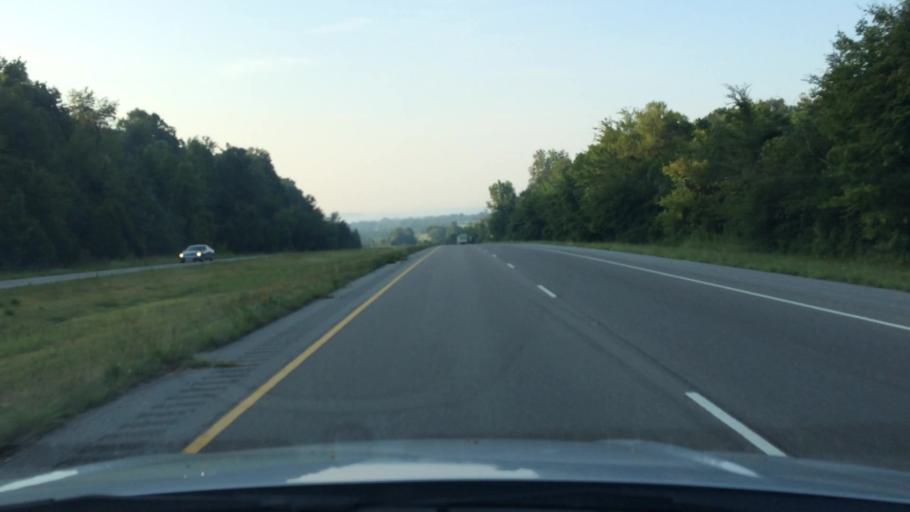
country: US
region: Tennessee
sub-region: Giles County
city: Pulaski
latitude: 35.1783
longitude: -87.0604
